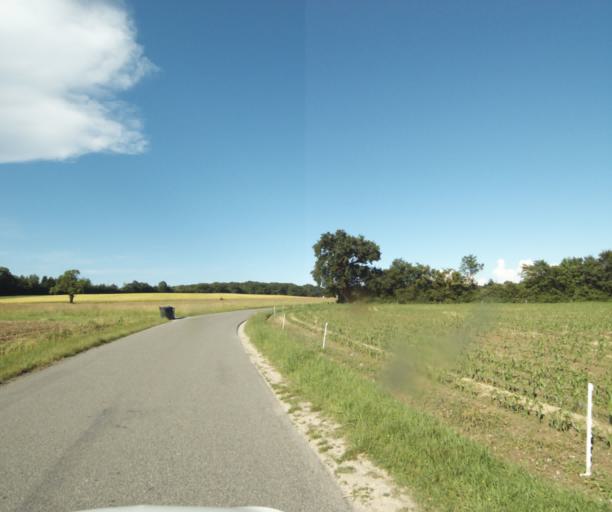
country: FR
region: Rhone-Alpes
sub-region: Departement de la Haute-Savoie
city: Massongy
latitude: 46.3518
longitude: 6.3342
